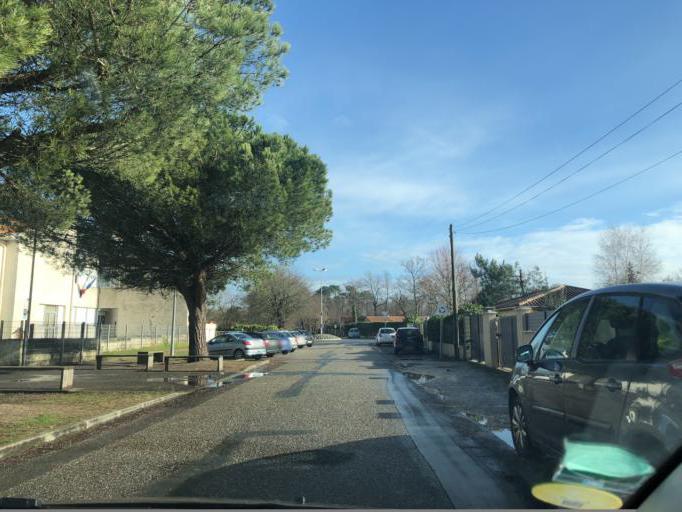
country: FR
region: Aquitaine
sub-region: Departement de la Gironde
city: Castelnau-de-Medoc
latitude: 45.0300
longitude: -0.7916
